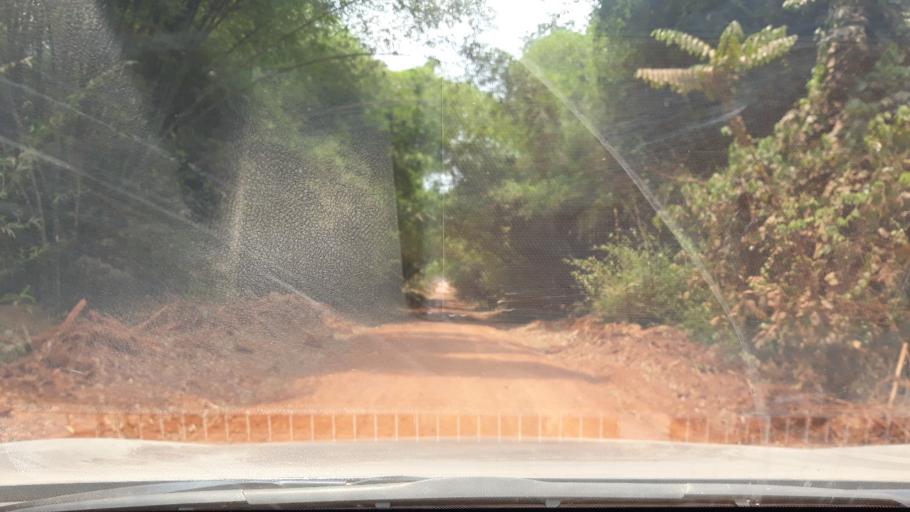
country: CD
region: Eastern Province
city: Buta
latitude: 2.2838
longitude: 25.1164
